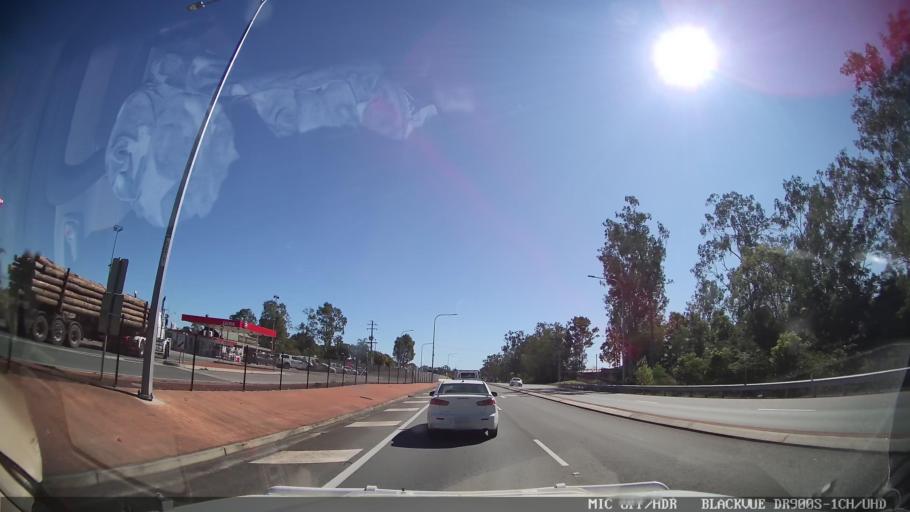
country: AU
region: Queensland
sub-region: Gympie Regional Council
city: Monkland
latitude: -26.2388
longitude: 152.6997
